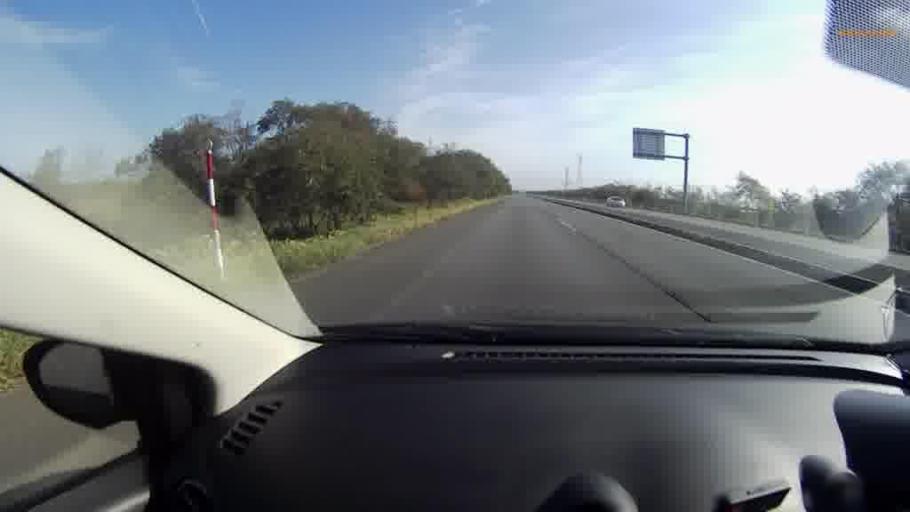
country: JP
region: Hokkaido
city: Kushiro
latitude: 43.0269
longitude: 144.2908
